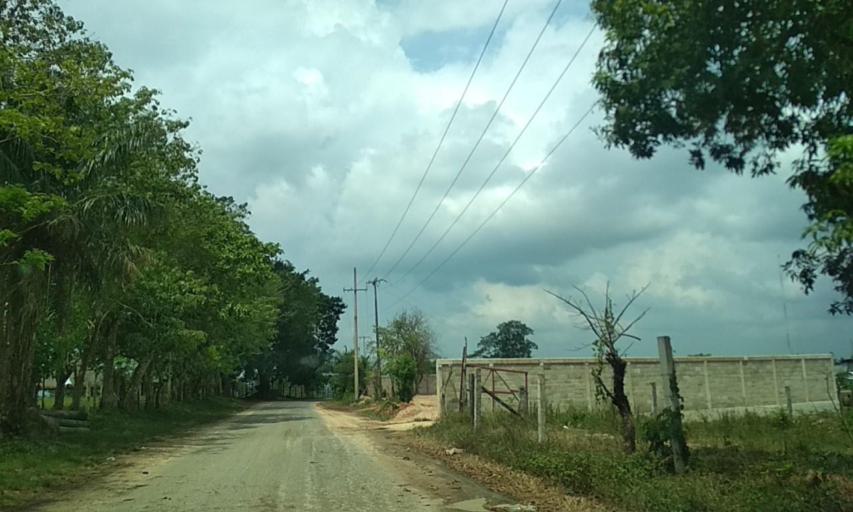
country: MX
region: Veracruz
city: Las Choapas
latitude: 17.8890
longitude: -94.1096
